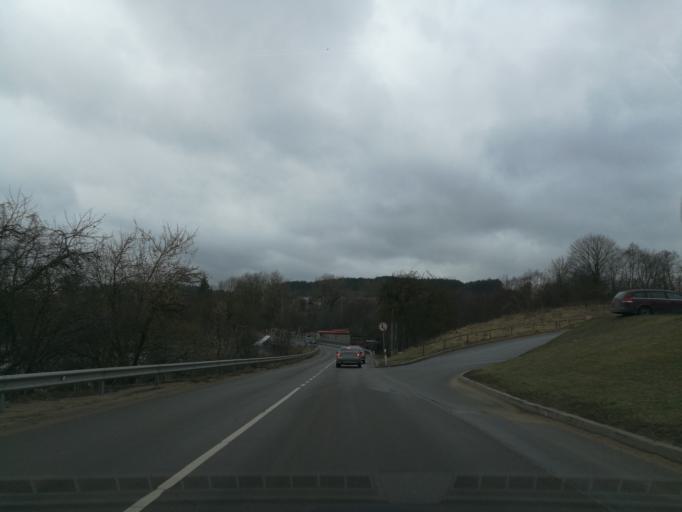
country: LT
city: Grigiskes
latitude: 54.6478
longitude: 25.1221
